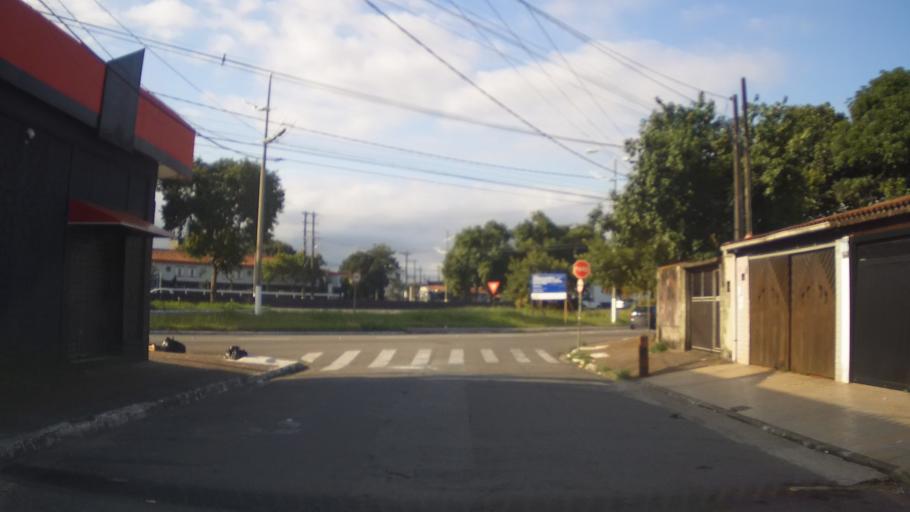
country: BR
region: Sao Paulo
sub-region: Praia Grande
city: Praia Grande
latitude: -24.0049
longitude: -46.4266
